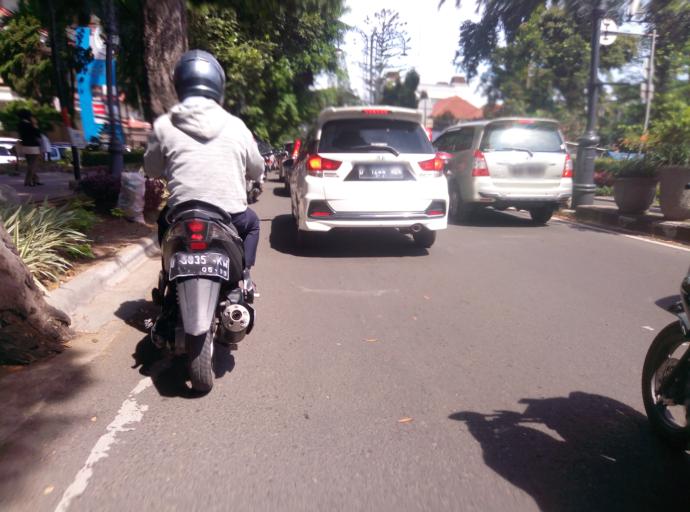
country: ID
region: West Java
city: Bandung
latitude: -6.8933
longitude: 107.6131
